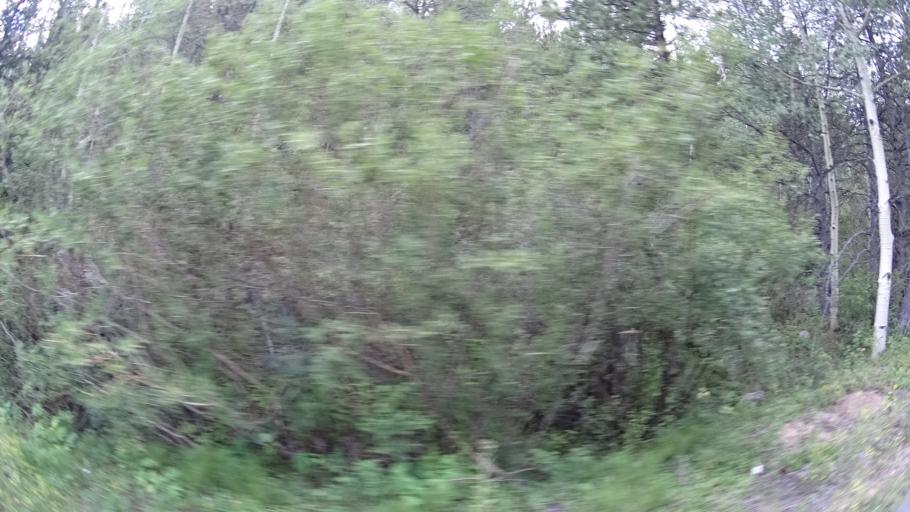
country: US
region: Colorado
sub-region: El Paso County
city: Cascade-Chipita Park
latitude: 38.9017
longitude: -105.0022
